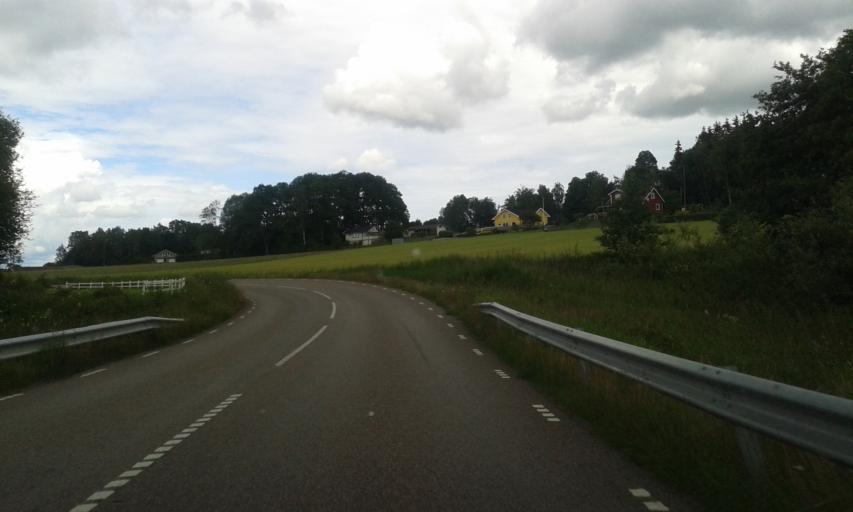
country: SE
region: Vaestra Goetaland
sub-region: Lilla Edets Kommun
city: Lilla Edet
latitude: 58.1163
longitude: 12.1155
